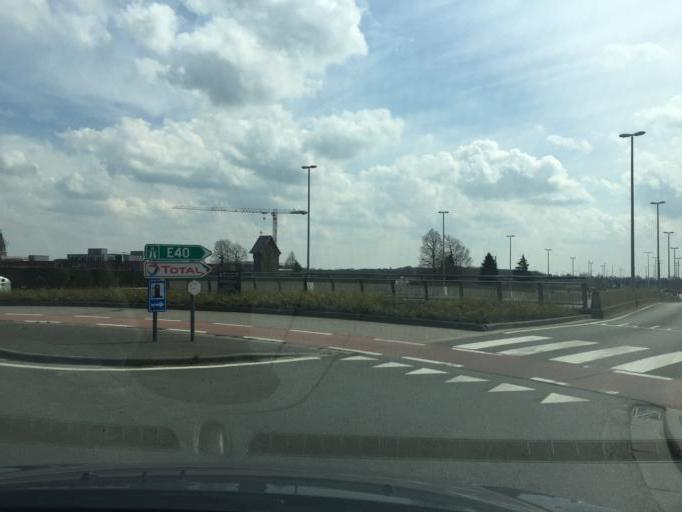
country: BE
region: Flanders
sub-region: Provincie Oost-Vlaanderen
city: Aalter
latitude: 51.0832
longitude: 3.4440
